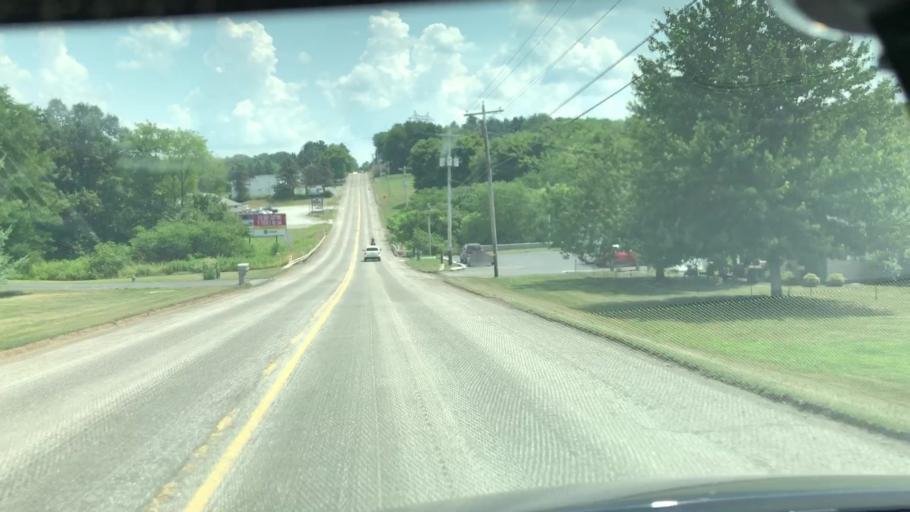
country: US
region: Pennsylvania
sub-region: Butler County
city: Saxonburg
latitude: 40.7942
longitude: -79.8150
